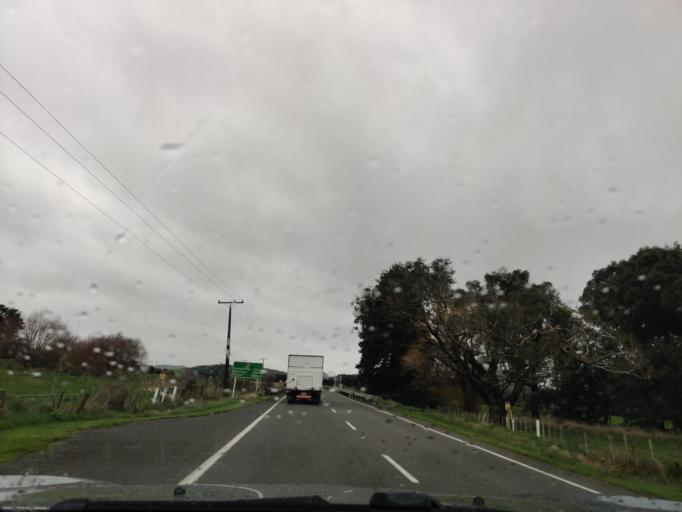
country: NZ
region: Manawatu-Wanganui
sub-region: Palmerston North City
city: Palmerston North
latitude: -40.3408
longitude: 175.8809
